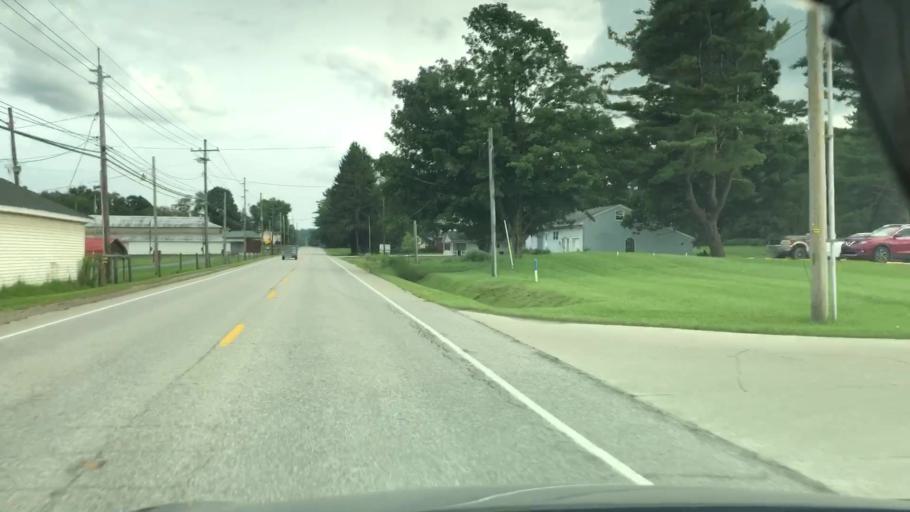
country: US
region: Pennsylvania
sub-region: Erie County
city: Union City
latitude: 42.0138
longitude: -79.8158
